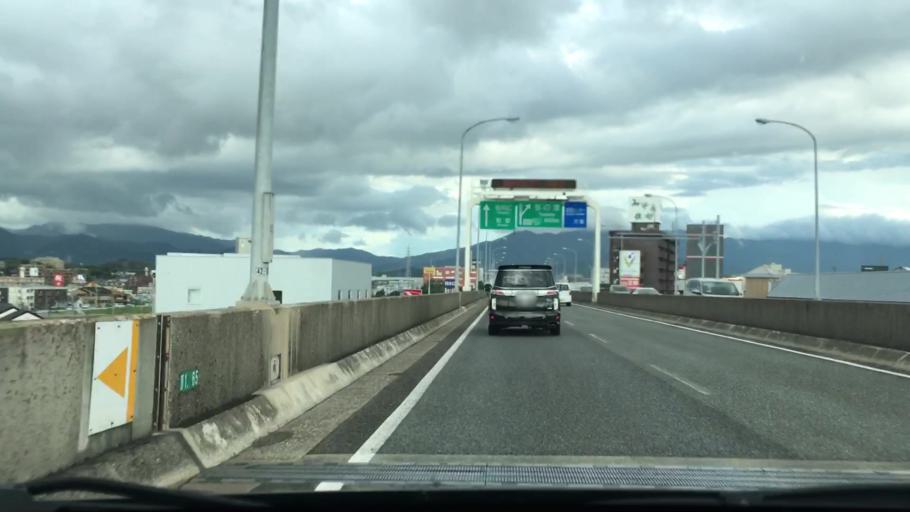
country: JP
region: Fukuoka
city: Fukuoka-shi
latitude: 33.6300
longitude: 130.4416
